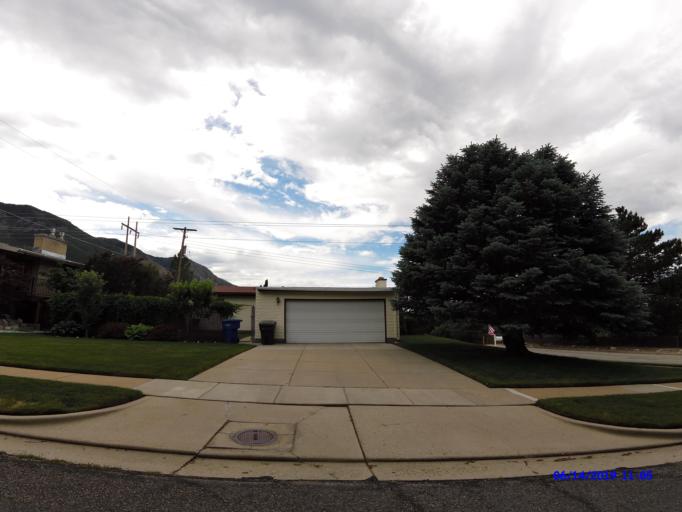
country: US
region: Utah
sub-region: Weber County
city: Ogden
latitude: 41.2440
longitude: -111.9379
